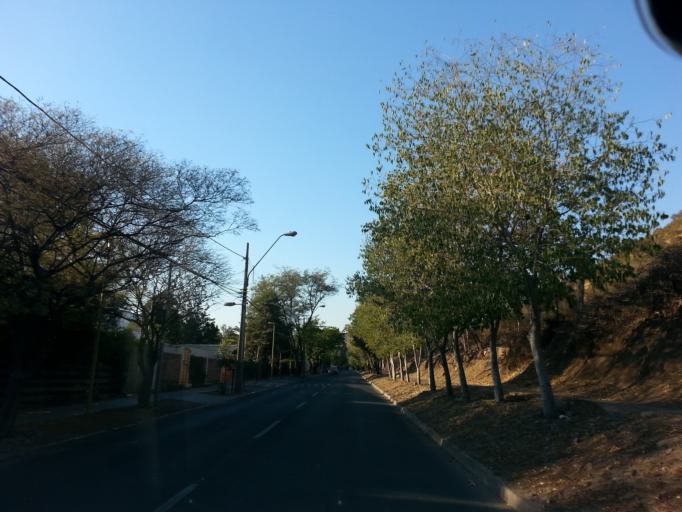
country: CL
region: Santiago Metropolitan
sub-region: Provincia de Santiago
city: Villa Presidente Frei, Nunoa, Santiago, Chile
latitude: -33.3994
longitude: -70.5401
